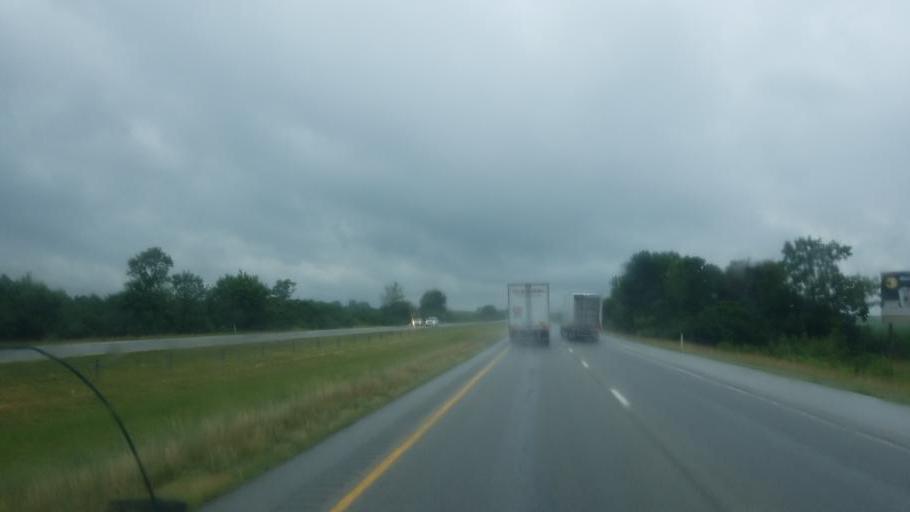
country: US
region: Indiana
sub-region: Putnam County
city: Cloverdale
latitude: 39.5559
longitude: -86.6842
